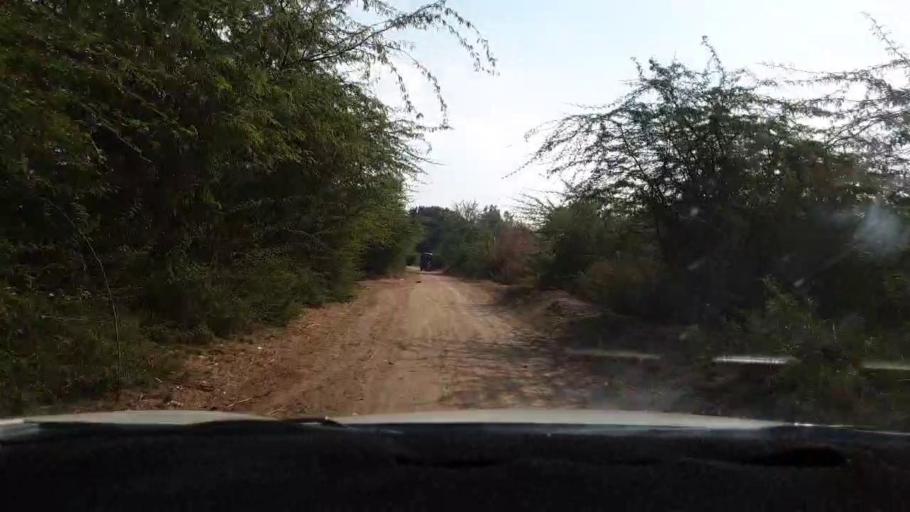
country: PK
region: Sindh
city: Berani
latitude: 25.7608
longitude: 68.9909
